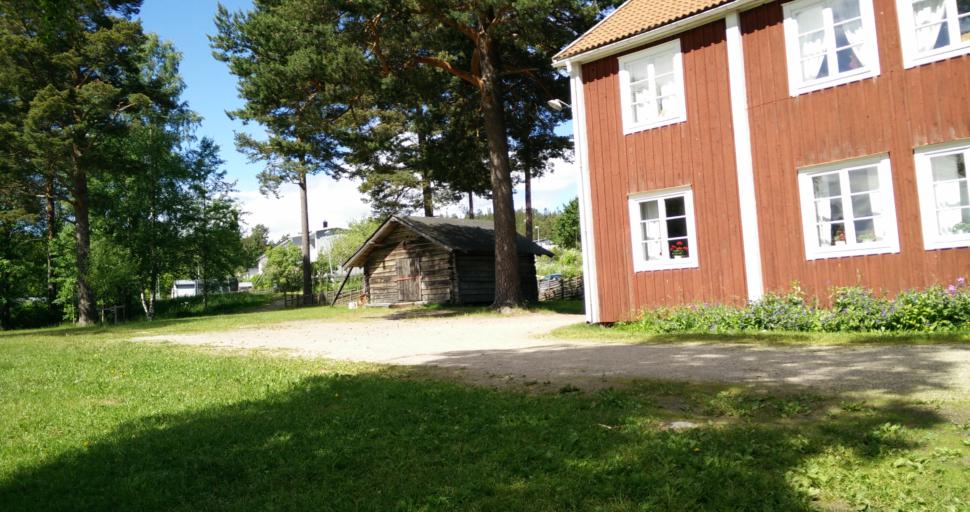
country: SE
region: Vaesternorrland
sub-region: Sundsvalls Kommun
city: Nolby
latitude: 62.2755
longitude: 17.3681
